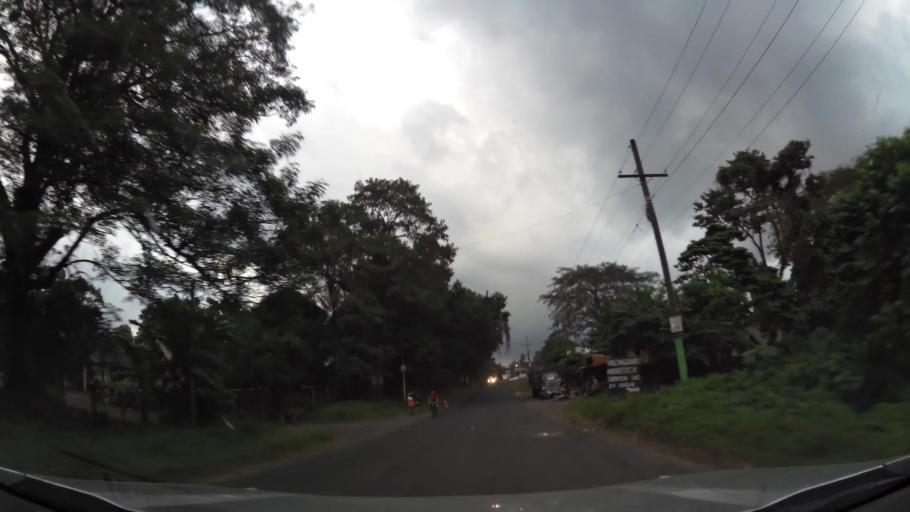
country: GT
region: Escuintla
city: Santa Lucia Cotzumalguapa
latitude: 14.3116
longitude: -91.0435
